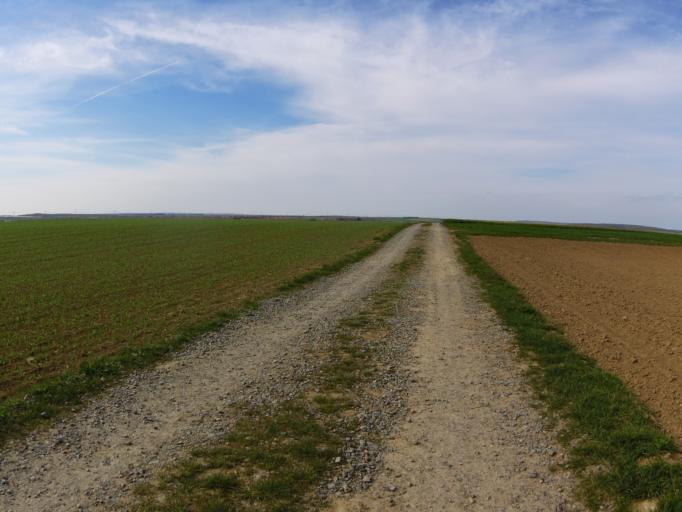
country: DE
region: Bavaria
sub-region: Regierungsbezirk Unterfranken
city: Mainstockheim
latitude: 49.7967
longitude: 10.1359
